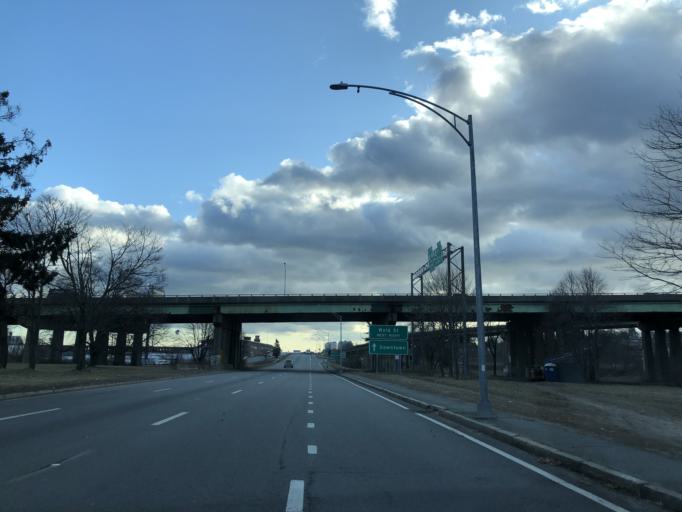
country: US
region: Massachusetts
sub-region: Bristol County
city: New Bedford
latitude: 41.6551
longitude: -70.9289
